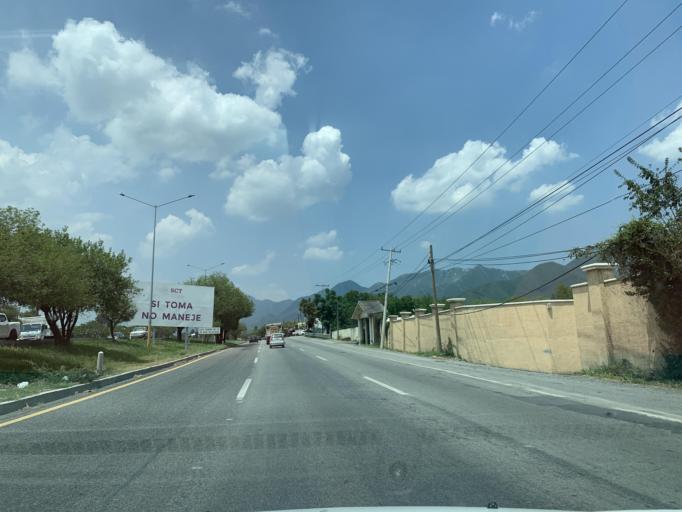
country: MX
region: Nuevo Leon
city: Santiago
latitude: 25.4373
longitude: -100.1531
